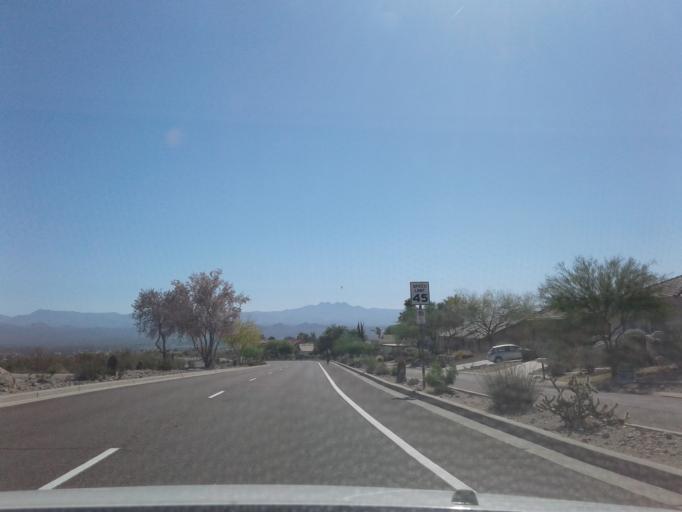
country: US
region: Arizona
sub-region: Maricopa County
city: Fountain Hills
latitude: 33.6033
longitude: -111.7549
